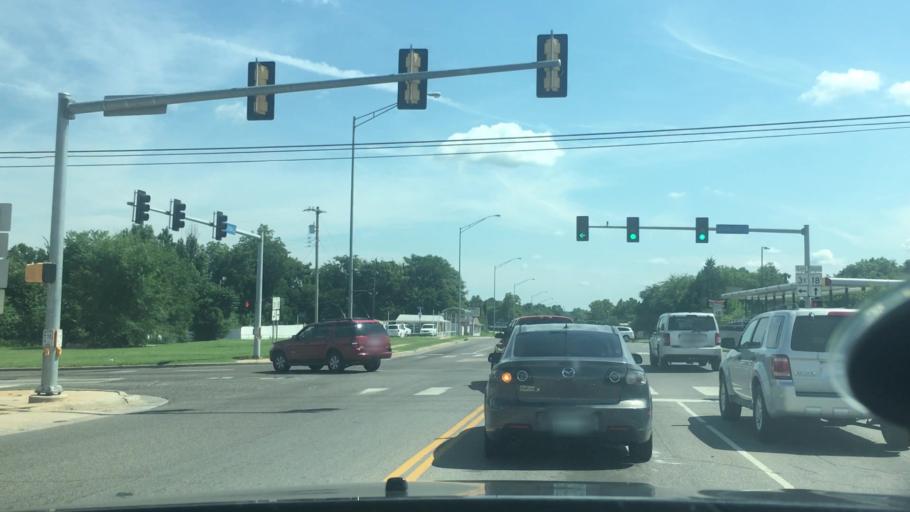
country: US
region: Oklahoma
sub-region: Pottawatomie County
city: Shawnee
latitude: 35.3331
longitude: -96.9121
